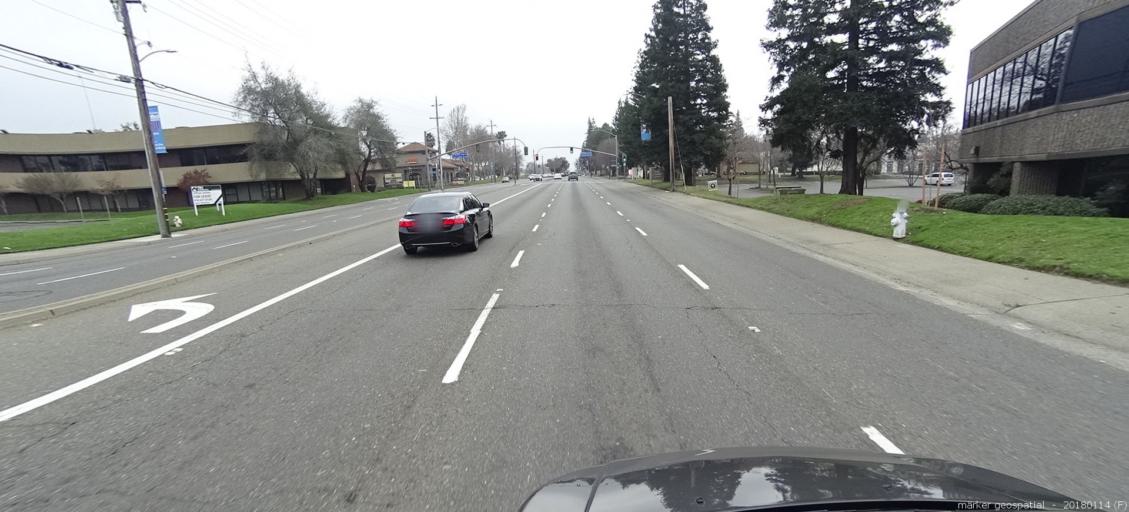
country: US
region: California
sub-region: Sacramento County
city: Gold River
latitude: 38.5989
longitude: -121.2658
